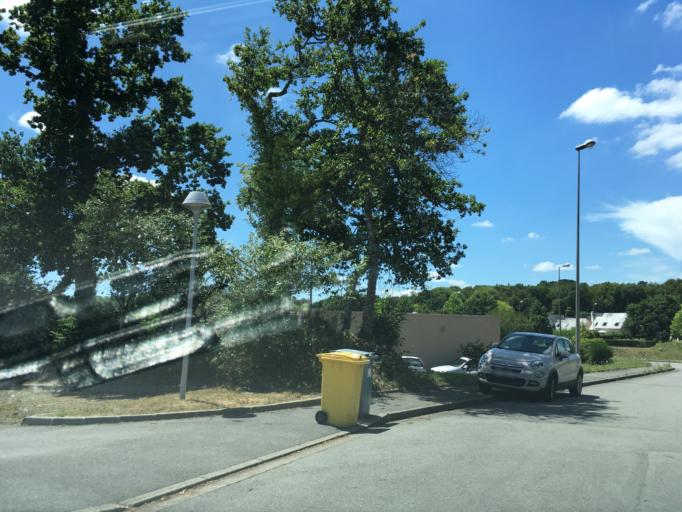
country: FR
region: Brittany
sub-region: Departement du Finistere
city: Quimper
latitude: 47.9783
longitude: -4.0829
